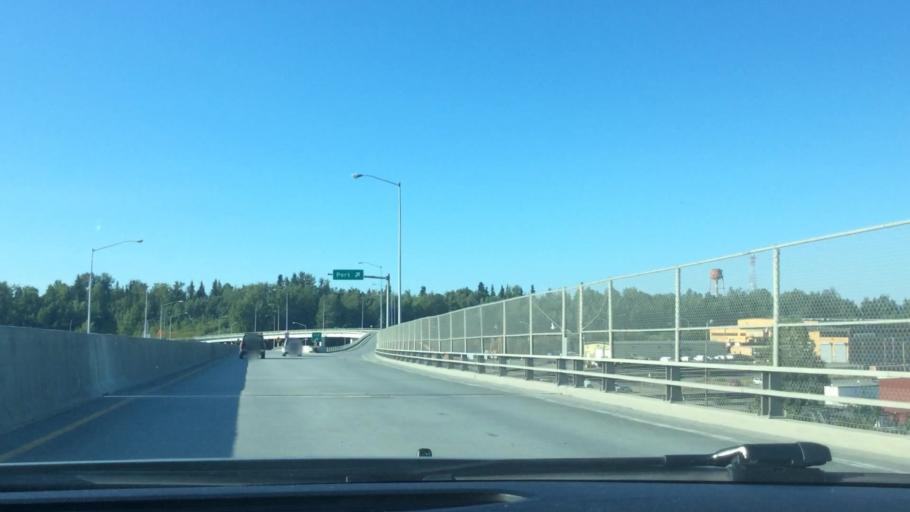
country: US
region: Alaska
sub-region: Anchorage Municipality
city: Anchorage
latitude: 61.2235
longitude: -149.8851
